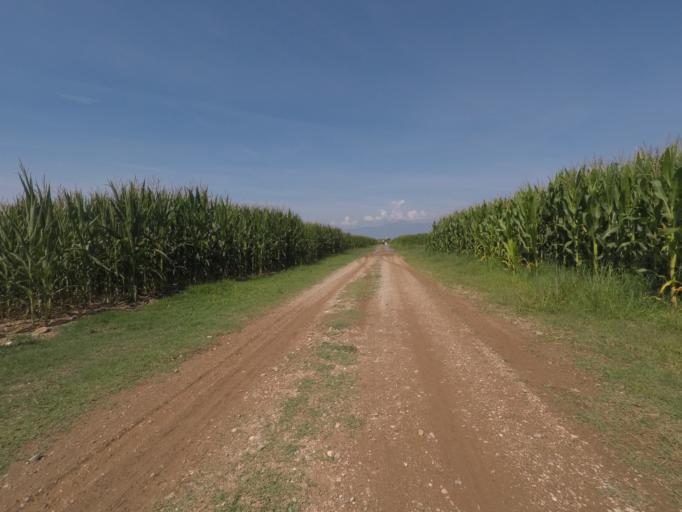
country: IT
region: Friuli Venezia Giulia
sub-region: Provincia di Udine
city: Dignano
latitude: 46.0830
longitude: 12.9622
